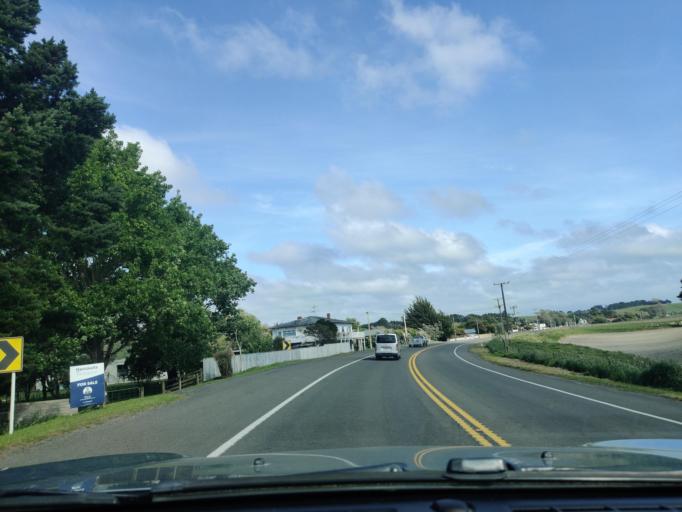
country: NZ
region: Manawatu-Wanganui
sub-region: Wanganui District
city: Wanganui
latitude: -40.0352
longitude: 175.2116
